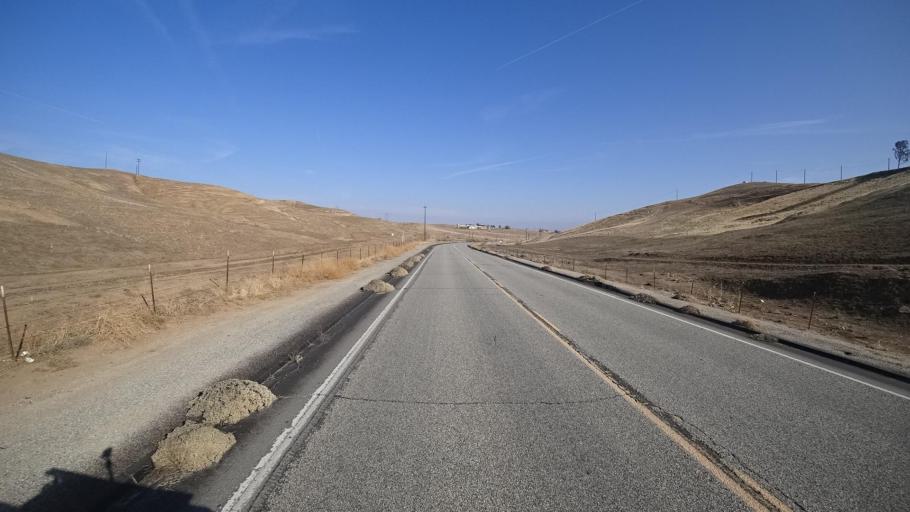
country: US
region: California
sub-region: Kern County
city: Oildale
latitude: 35.4974
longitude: -118.9955
